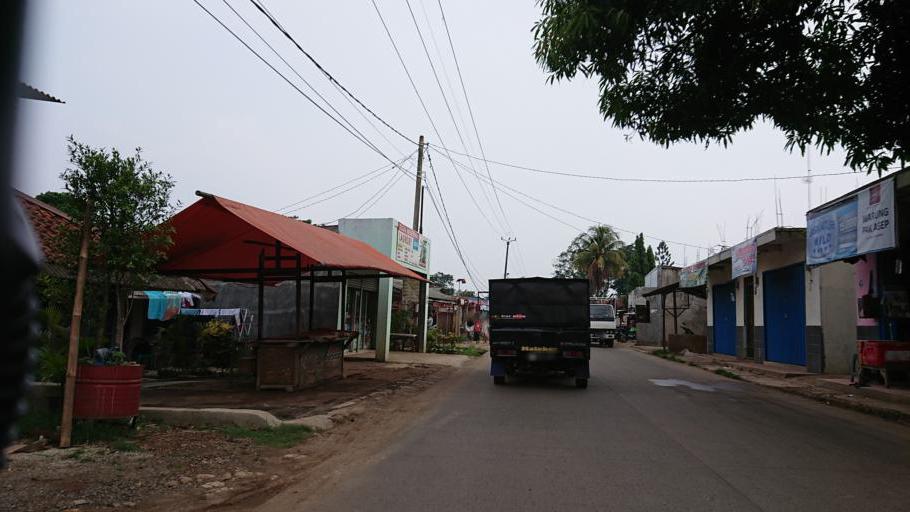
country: ID
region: West Java
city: Parung
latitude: -6.3974
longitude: 106.6874
